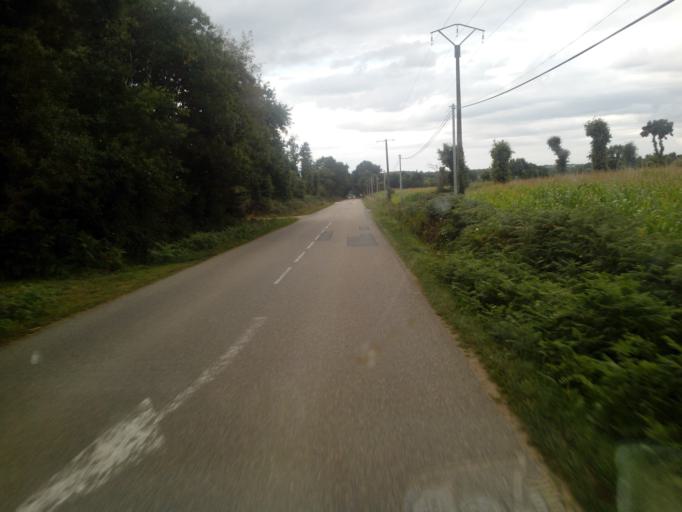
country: FR
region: Brittany
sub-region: Departement d'Ille-et-Vilaine
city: Maxent
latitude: 47.9788
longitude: -2.0236
